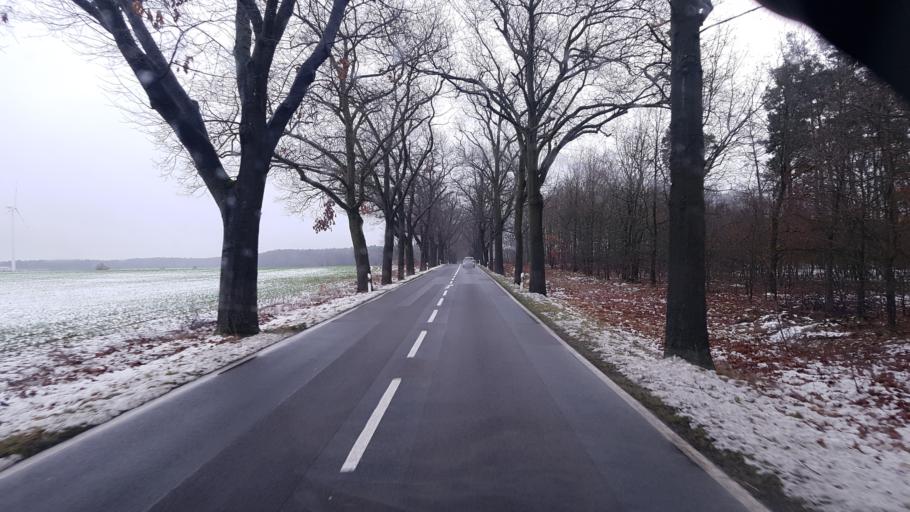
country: DE
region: Brandenburg
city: Schenkendobern
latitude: 51.9645
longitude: 14.5868
